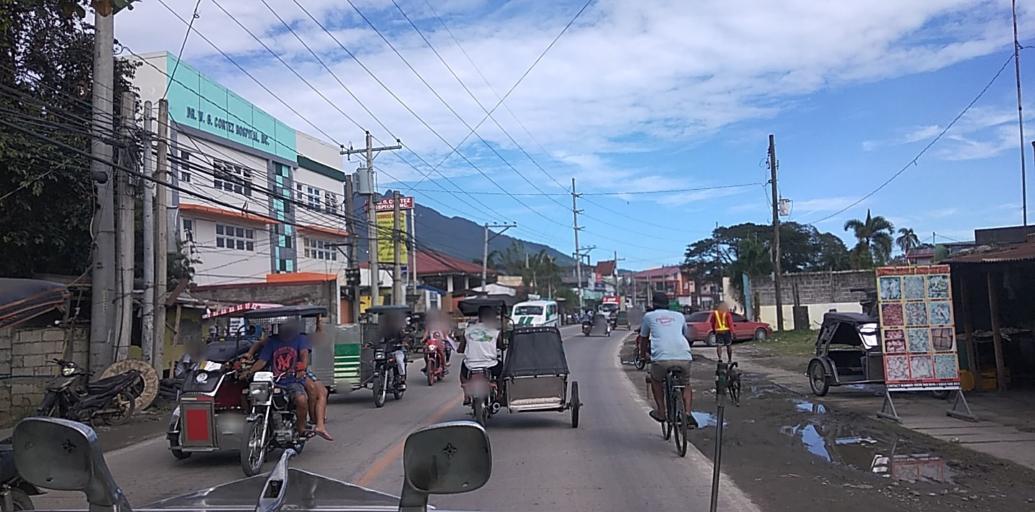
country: PH
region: Central Luzon
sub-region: Province of Pampanga
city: Arayat
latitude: 15.1475
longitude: 120.7665
